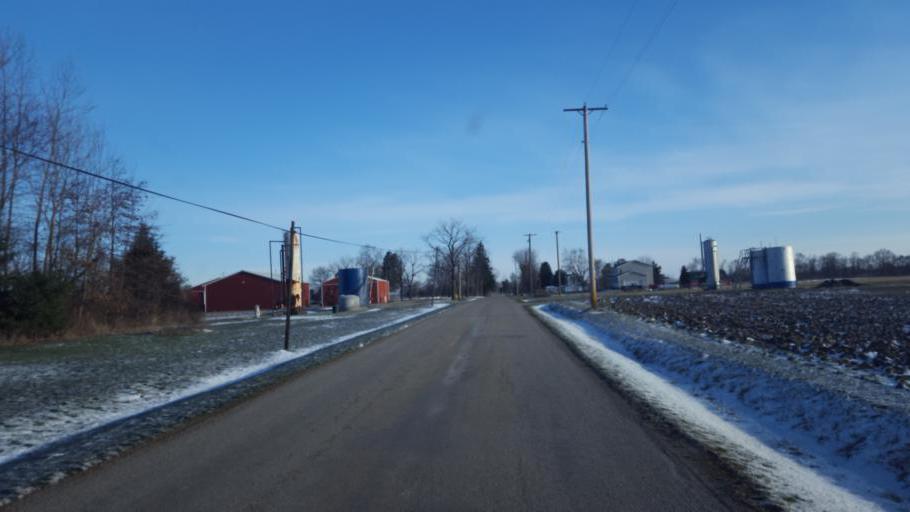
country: US
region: Ohio
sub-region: Morrow County
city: Cardington
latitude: 40.5747
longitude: -82.9190
